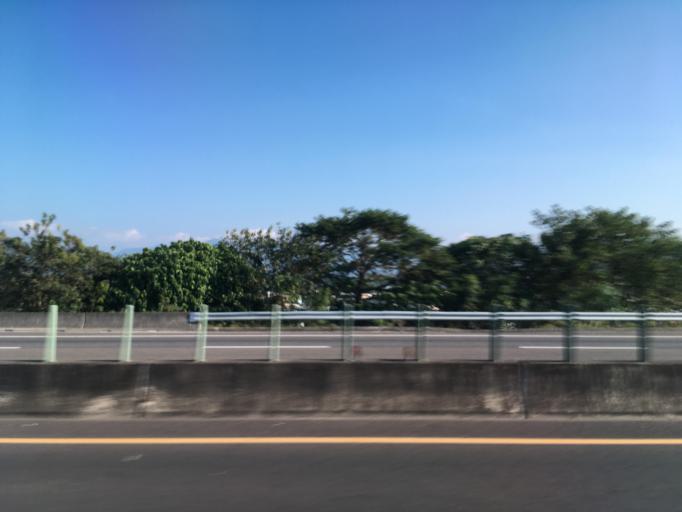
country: TW
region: Taiwan
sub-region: Chiayi
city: Jiayi Shi
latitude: 23.4394
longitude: 120.4793
